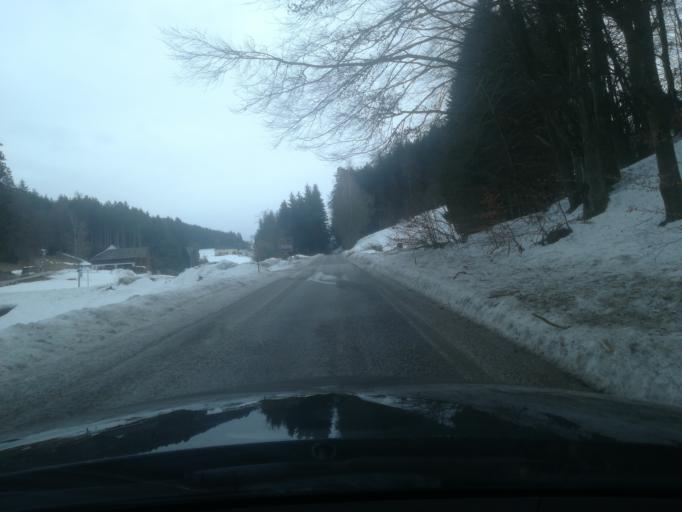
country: AT
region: Upper Austria
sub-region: Politischer Bezirk Perg
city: Perg
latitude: 48.4125
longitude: 14.6626
